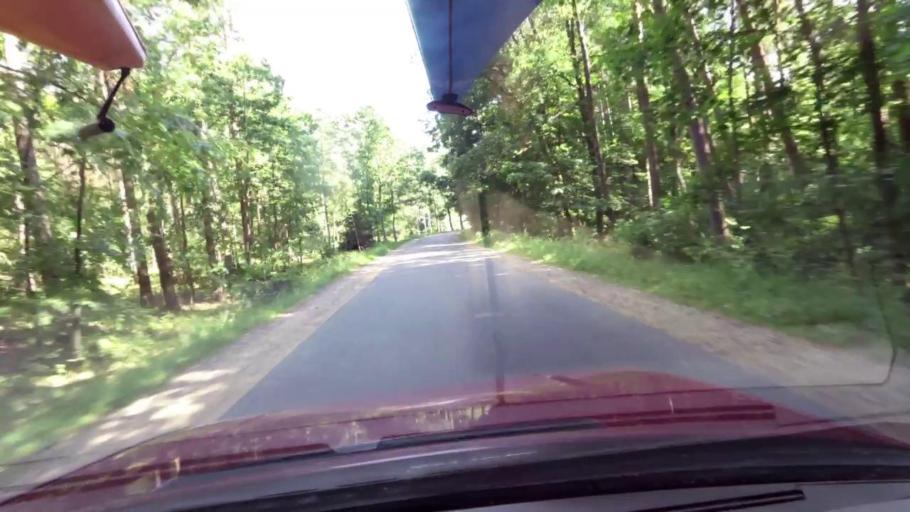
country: PL
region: Pomeranian Voivodeship
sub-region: Powiat slupski
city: Kepice
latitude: 54.1342
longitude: 16.9317
